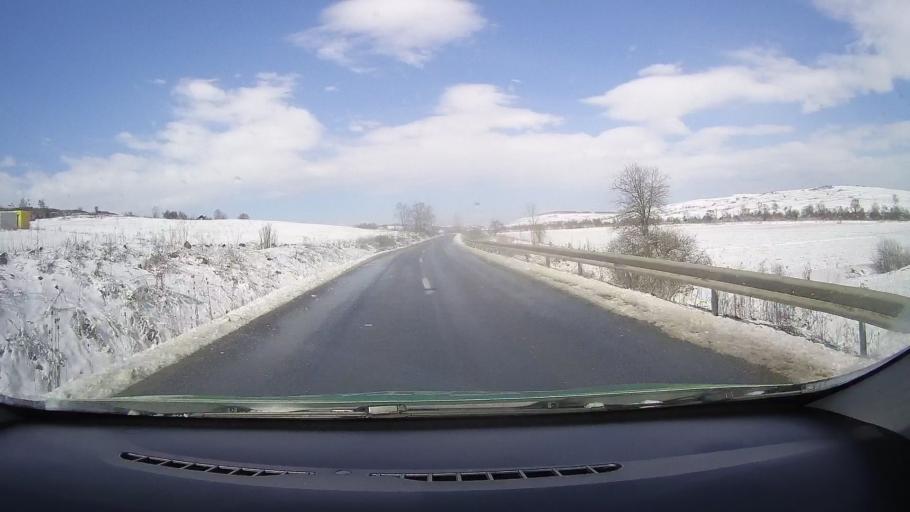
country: RO
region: Sibiu
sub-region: Comuna Nocrich
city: Nocrich
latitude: 45.9039
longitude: 24.4644
